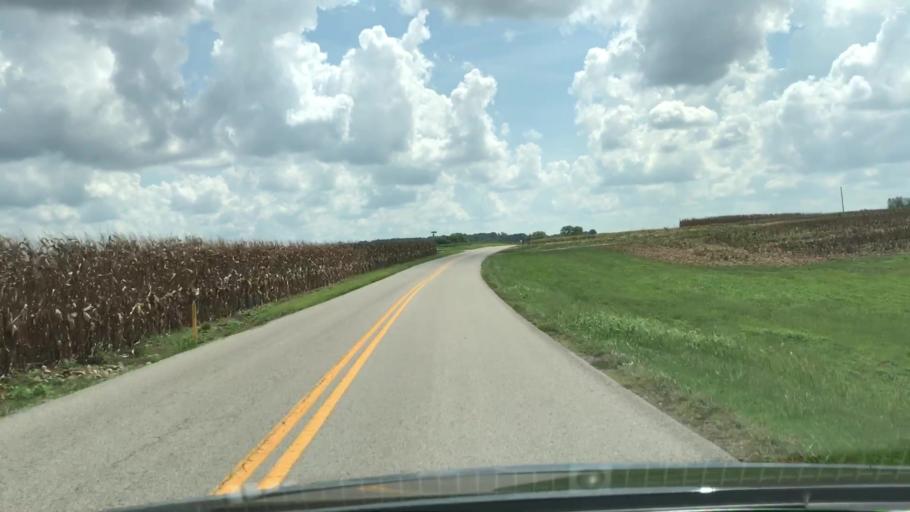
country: US
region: Kentucky
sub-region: Todd County
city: Guthrie
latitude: 36.7088
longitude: -87.0489
